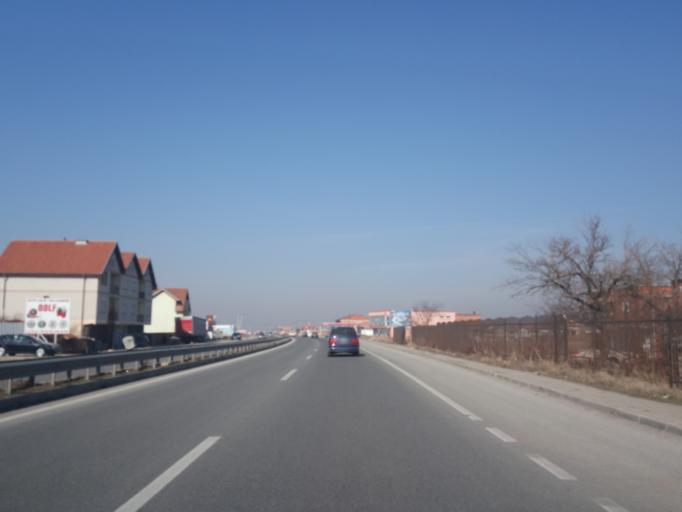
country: XK
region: Pristina
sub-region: Komuna e Obiliqit
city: Obiliq
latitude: 42.7454
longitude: 21.0475
